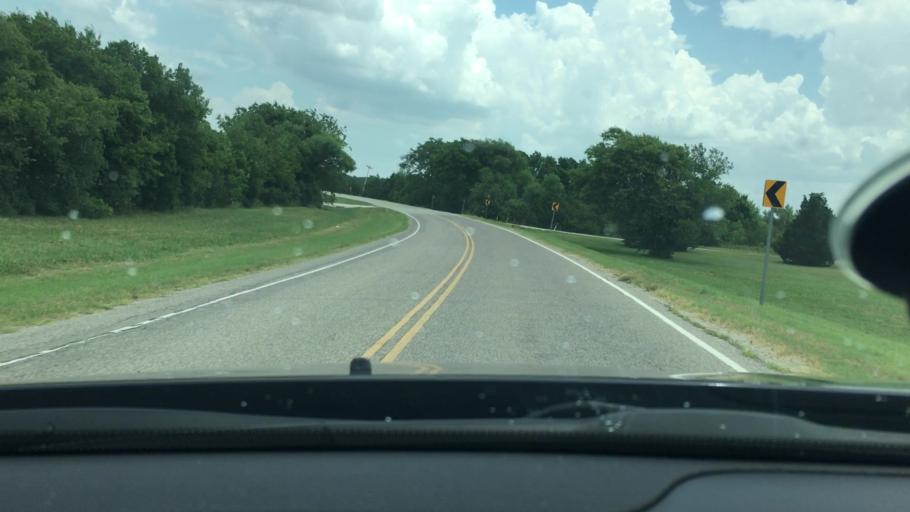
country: US
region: Oklahoma
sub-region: Love County
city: Marietta
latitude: 33.9407
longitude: -97.0407
